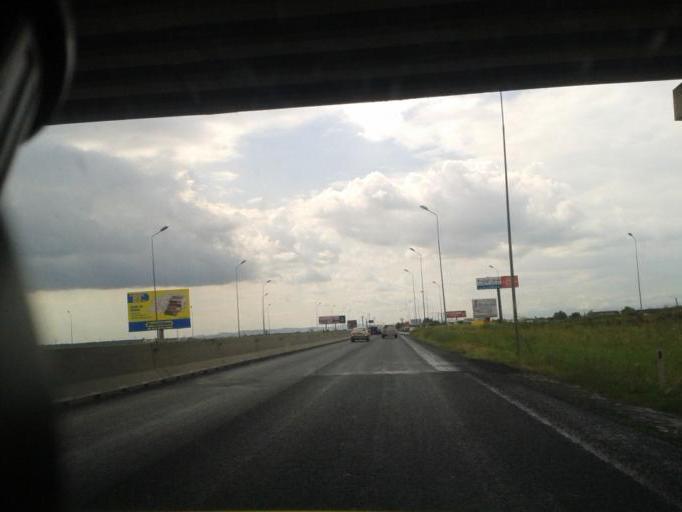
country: RO
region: Prahova
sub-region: Comuna Paulesti
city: Paulesti
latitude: 44.9712
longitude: 25.9560
